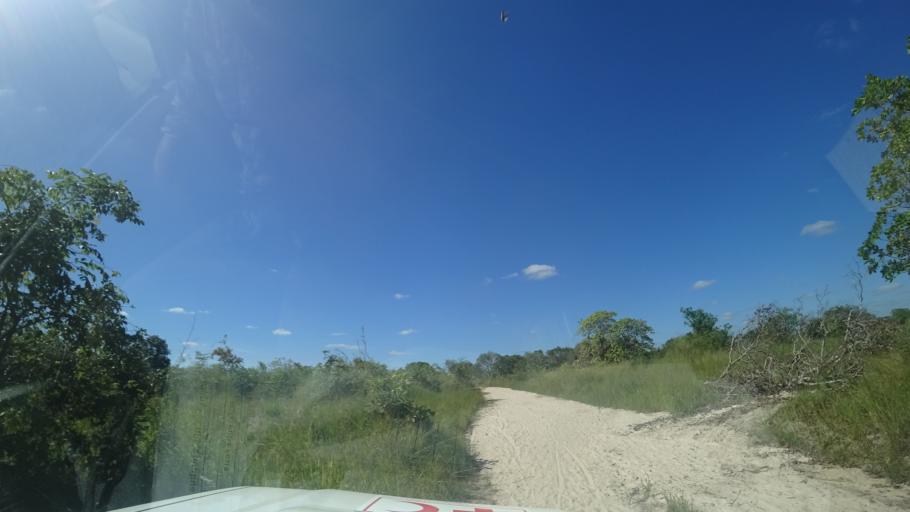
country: MZ
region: Sofala
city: Dondo
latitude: -19.4847
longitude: 34.6175
